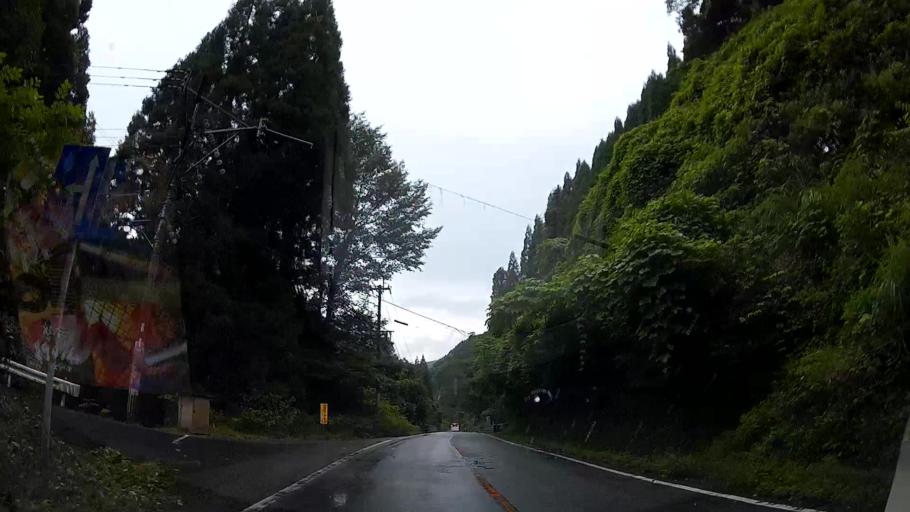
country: JP
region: Oita
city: Tsukawaki
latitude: 33.1648
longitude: 131.0436
